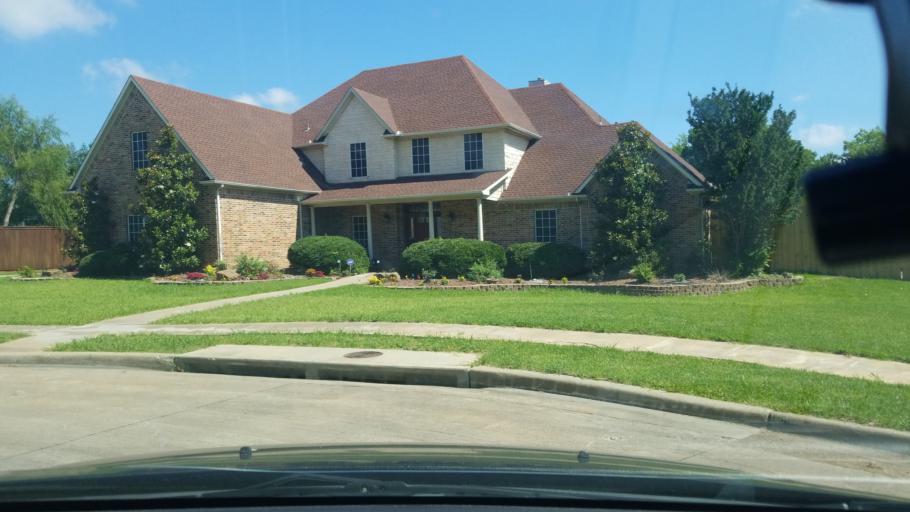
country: US
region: Texas
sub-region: Dallas County
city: Sunnyvale
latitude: 32.7896
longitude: -96.5736
